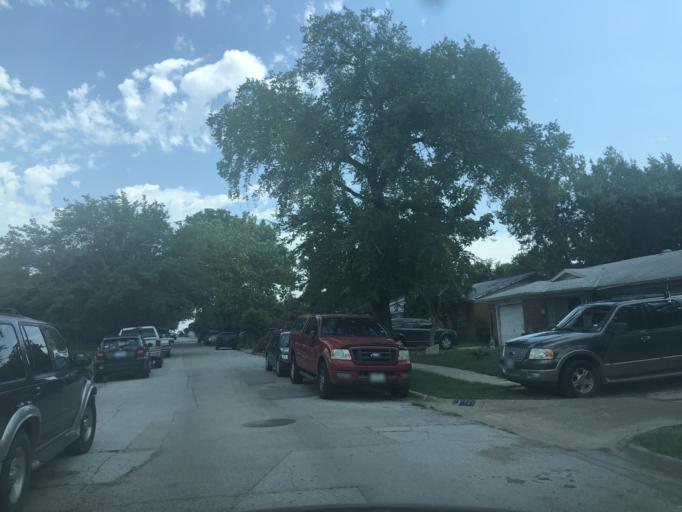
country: US
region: Texas
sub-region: Dallas County
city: Grand Prairie
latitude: 32.7215
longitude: -97.0082
